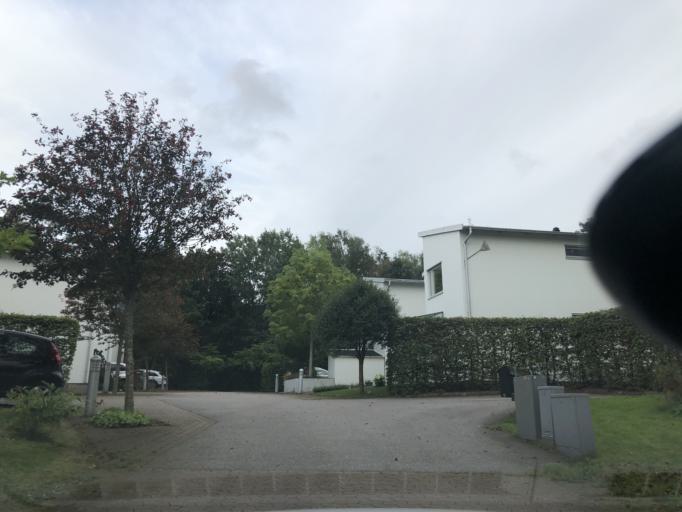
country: SE
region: Vaestra Goetaland
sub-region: Goteborg
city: Goeteborg
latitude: 57.7457
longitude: 11.9609
